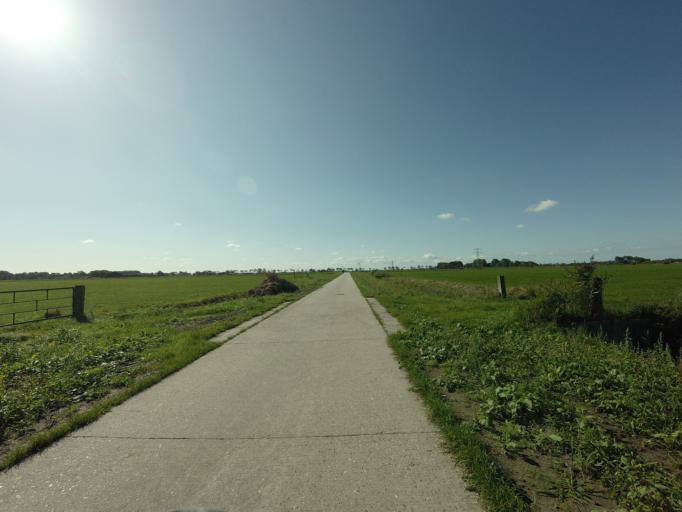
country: NL
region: Friesland
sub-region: Gemeente Leeuwarden
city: Wirdum
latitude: 53.1552
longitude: 5.7711
